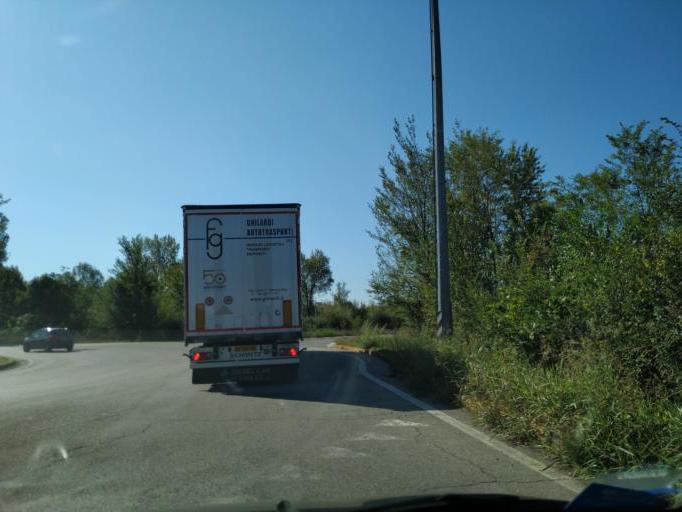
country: IT
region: Emilia-Romagna
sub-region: Provincia di Bologna
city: San Giovanni in Persiceto
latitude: 44.6453
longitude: 11.1709
